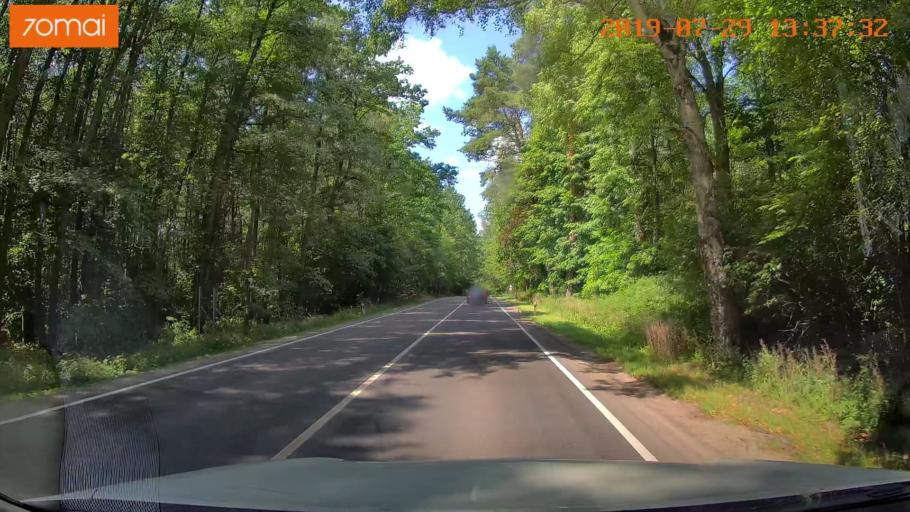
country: RU
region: Kaliningrad
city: Volochayevskoye
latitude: 54.7150
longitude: 20.1829
